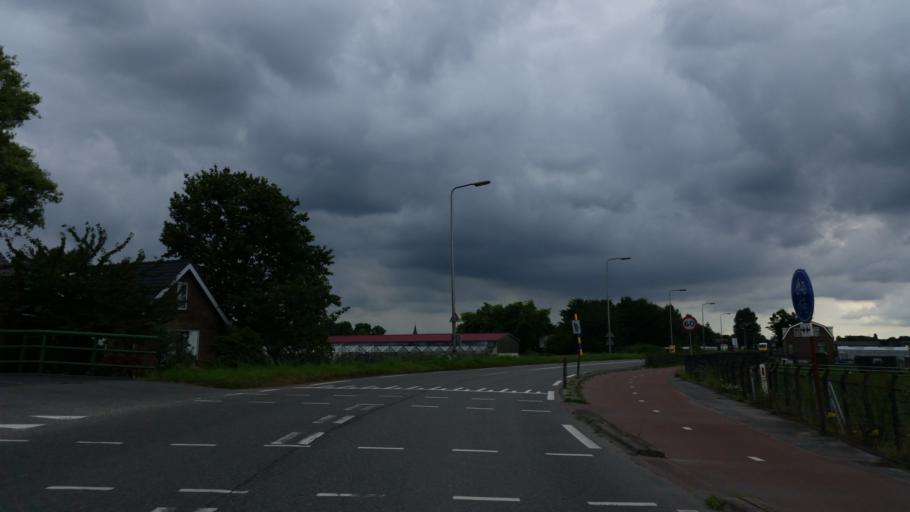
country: NL
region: South Holland
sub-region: Gemeente Pijnacker-Nootdorp
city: Pijnacker
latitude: 52.0335
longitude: 4.4471
